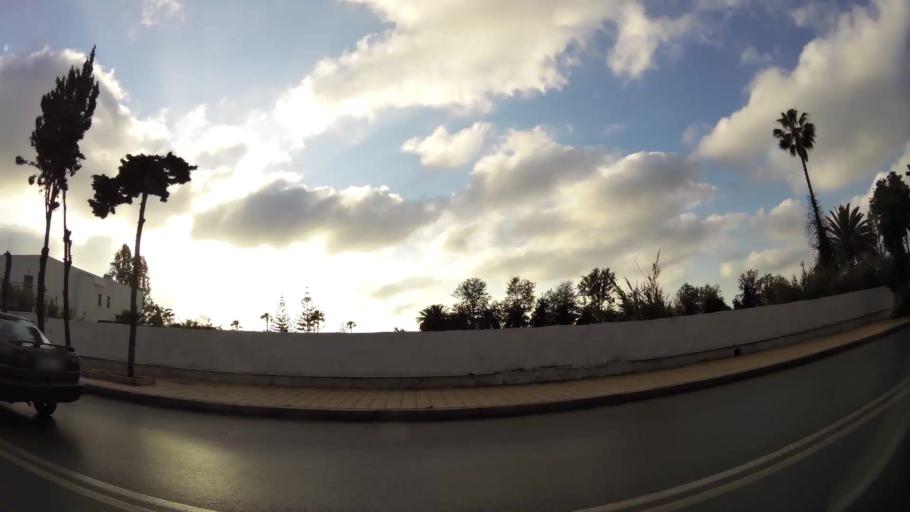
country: MA
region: Rabat-Sale-Zemmour-Zaer
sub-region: Rabat
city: Rabat
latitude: 33.9652
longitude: -6.8511
